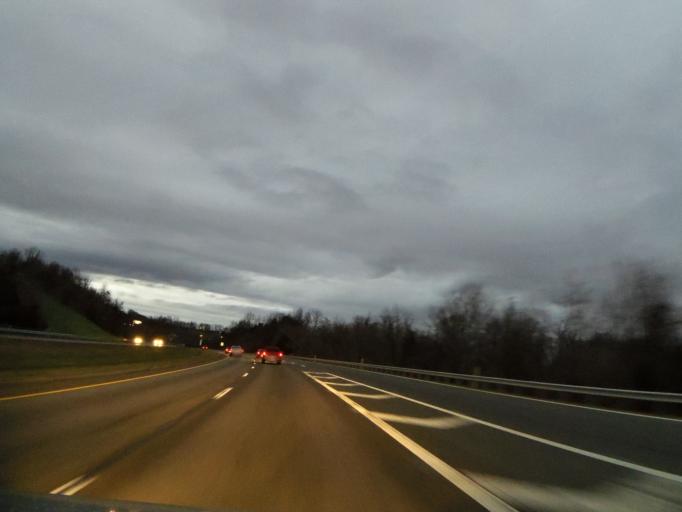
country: US
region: Tennessee
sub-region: Washington County
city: Oak Grove
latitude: 36.3834
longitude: -82.4286
